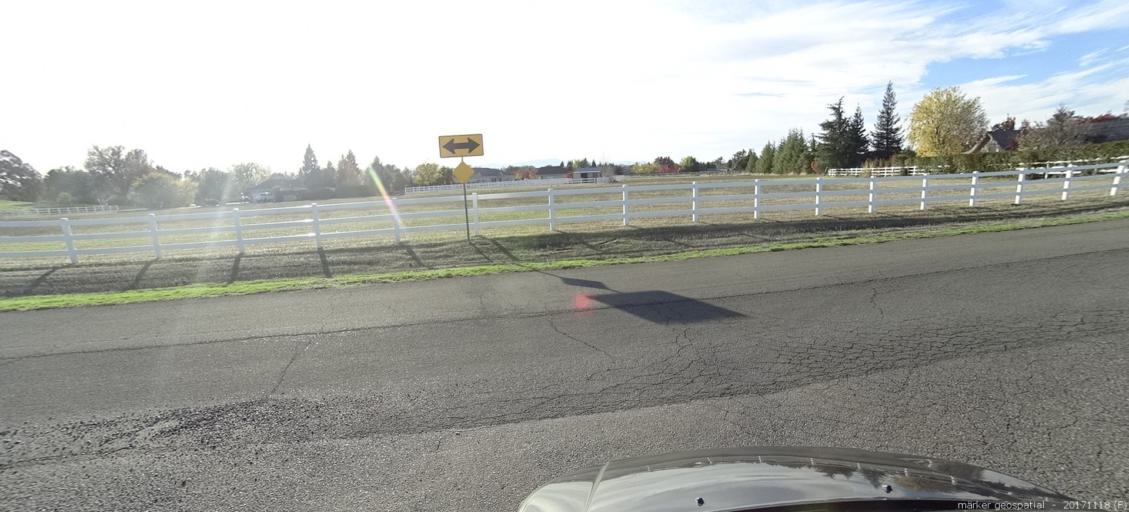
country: US
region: California
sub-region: Shasta County
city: Cottonwood
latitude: 40.3774
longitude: -122.3396
